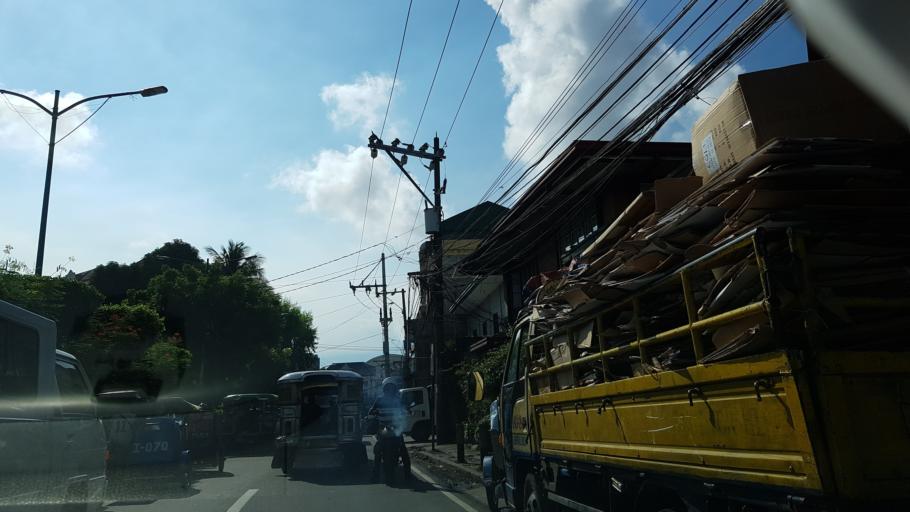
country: PH
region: Metro Manila
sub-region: Mandaluyong
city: Mandaluyong City
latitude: 14.5735
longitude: 121.0451
